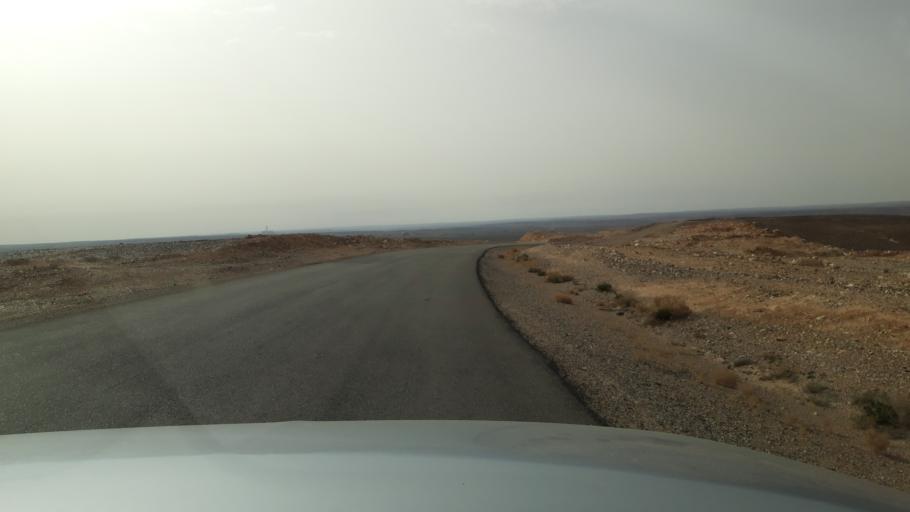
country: JO
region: Amman
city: Al Azraq ash Shamali
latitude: 31.2795
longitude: 36.5732
